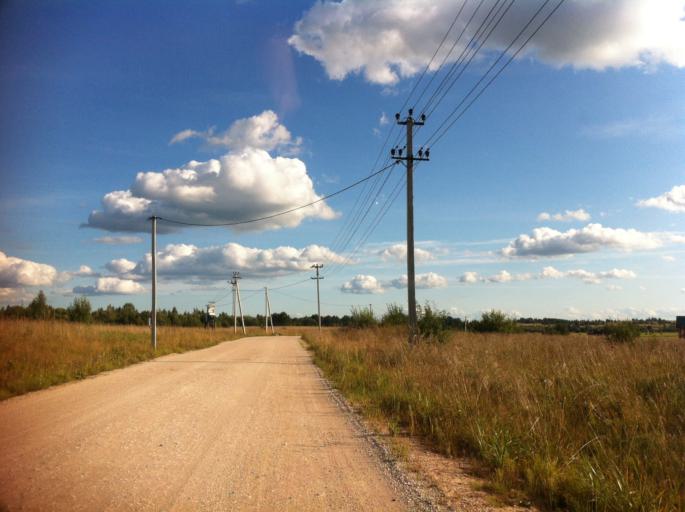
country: RU
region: Pskov
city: Izborsk
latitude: 57.8268
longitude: 27.9655
